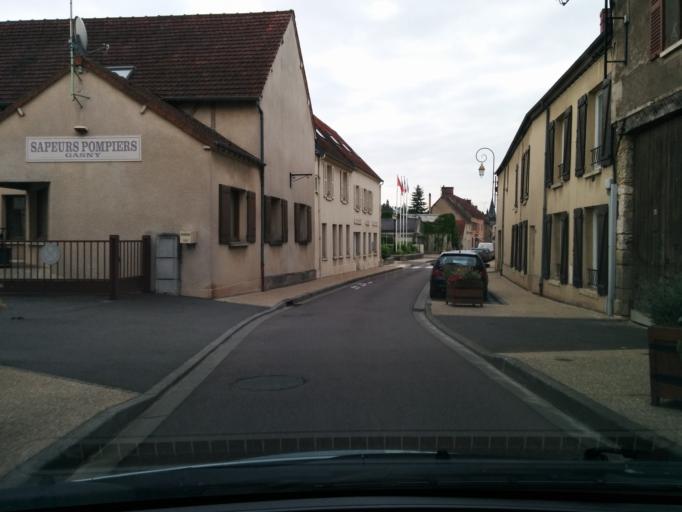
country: FR
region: Haute-Normandie
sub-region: Departement de l'Eure
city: Gasny
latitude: 49.0917
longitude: 1.6045
